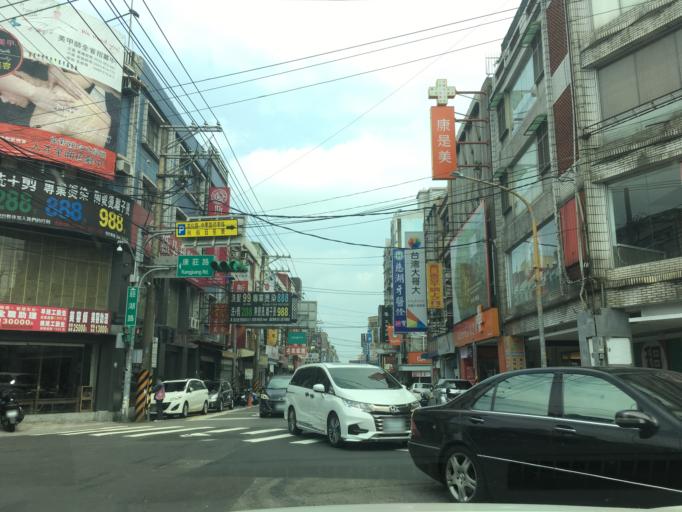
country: TW
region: Taiwan
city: Daxi
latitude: 24.8808
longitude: 121.2887
